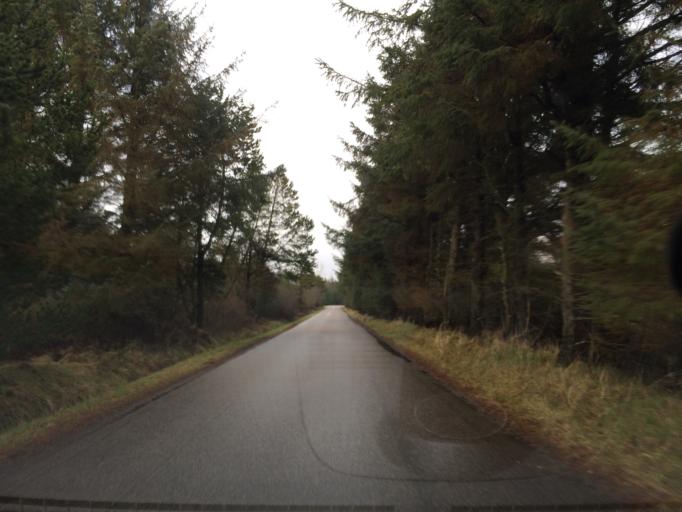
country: DK
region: Central Jutland
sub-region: Holstebro Kommune
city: Ulfborg
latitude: 56.2752
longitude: 8.1590
